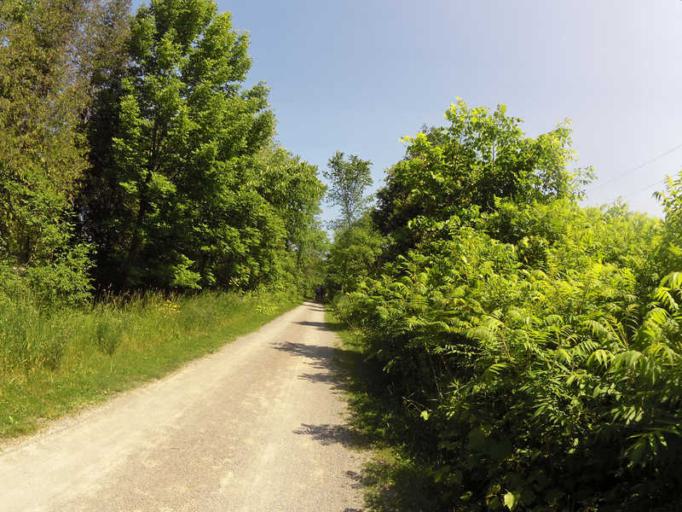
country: CA
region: Ontario
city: Peterborough
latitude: 44.3997
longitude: -78.2625
